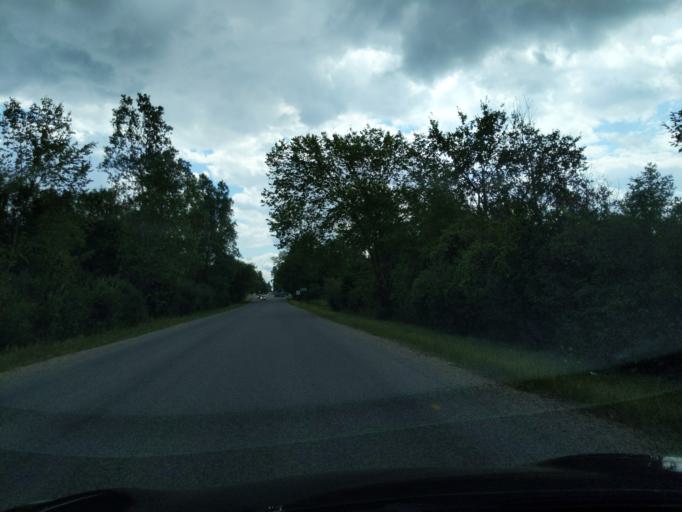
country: US
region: Michigan
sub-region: Ingham County
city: Holt
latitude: 42.6425
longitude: -84.5431
